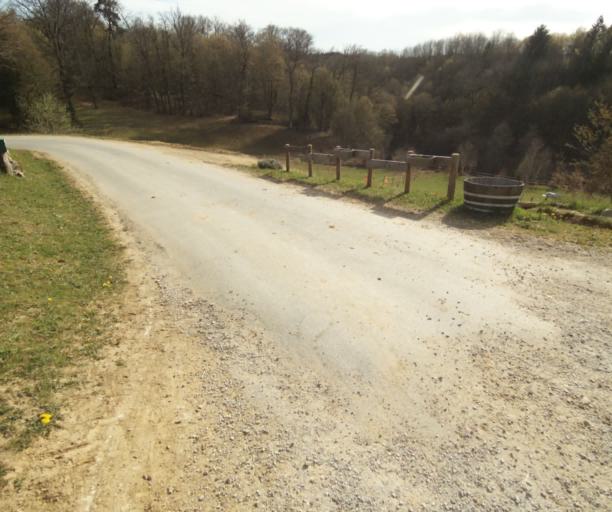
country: FR
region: Limousin
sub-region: Departement de la Correze
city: Saint-Clement
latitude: 45.3185
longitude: 1.7177
